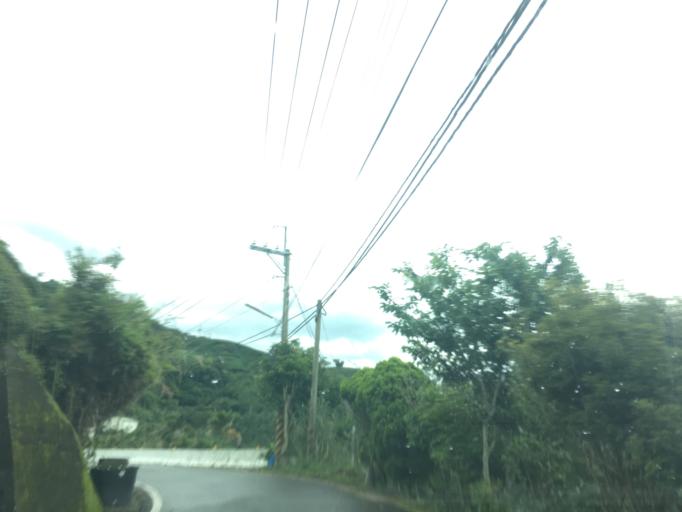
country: TW
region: Taiwan
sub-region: Yunlin
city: Douliu
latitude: 23.5612
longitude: 120.6590
